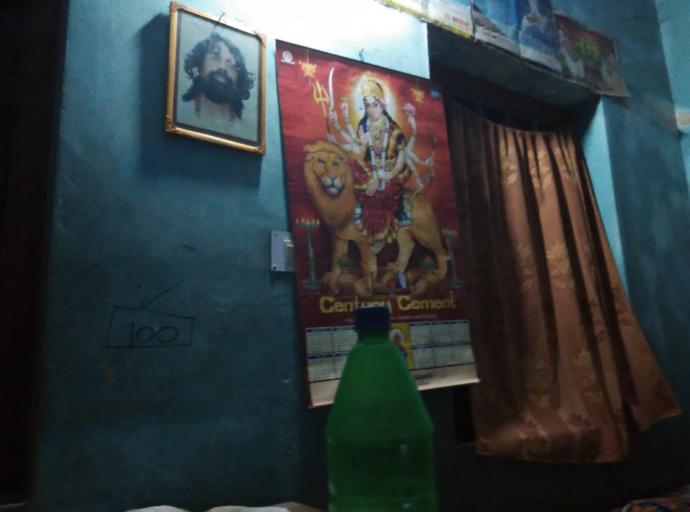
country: IN
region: Odisha
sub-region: Cuttack
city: Cuttack
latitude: 20.4501
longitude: 85.9247
